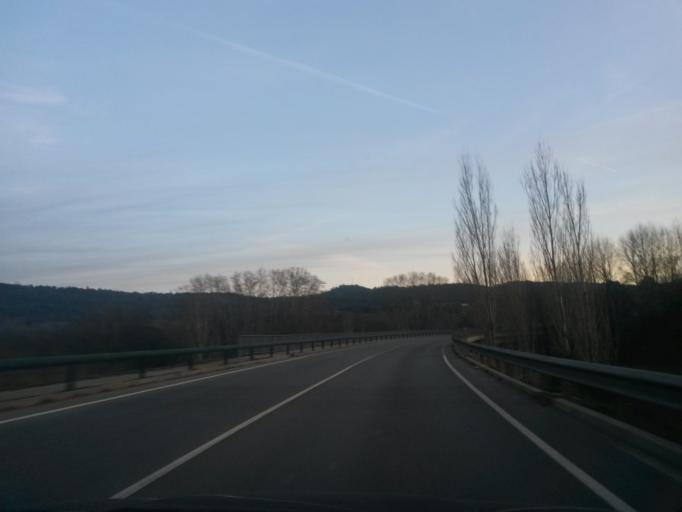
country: ES
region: Catalonia
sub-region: Provincia de Girona
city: Girona
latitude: 41.9665
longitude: 2.8413
